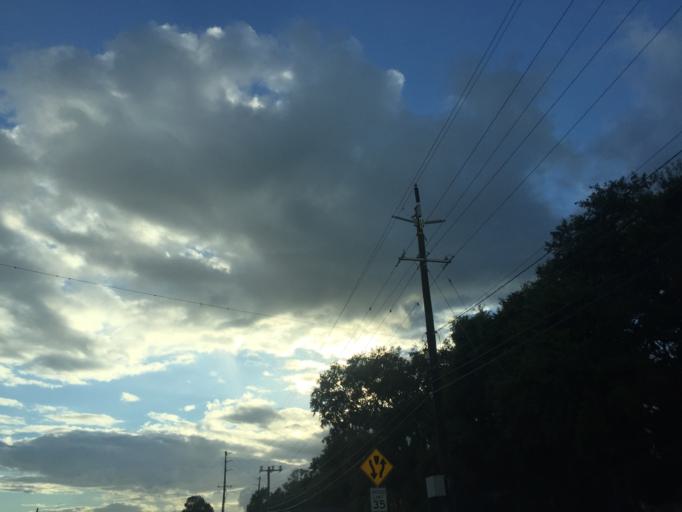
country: US
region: Georgia
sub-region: Chatham County
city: Tybee Island
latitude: 32.0199
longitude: -80.8591
